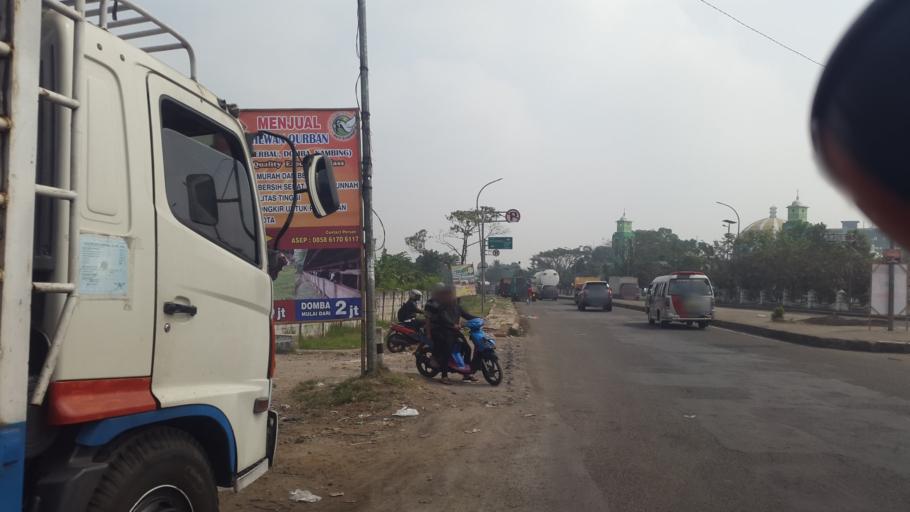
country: ID
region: West Java
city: Sukabumi
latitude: -6.9075
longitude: 106.8734
